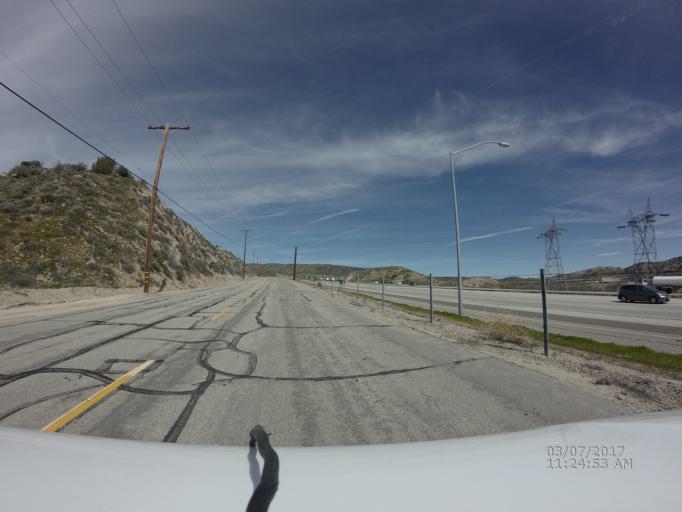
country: US
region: California
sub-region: Kern County
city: Lebec
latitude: 34.7523
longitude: -118.7962
